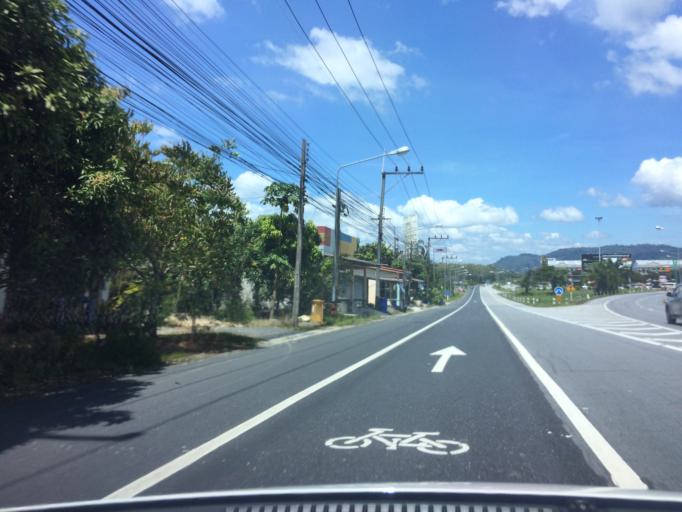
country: TH
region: Phangnga
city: Thai Mueang
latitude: 8.2435
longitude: 98.2975
